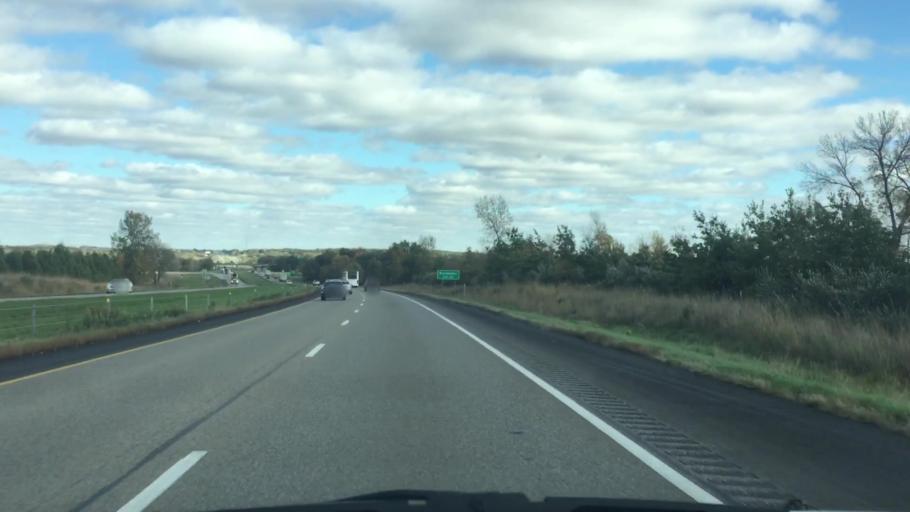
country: US
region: Iowa
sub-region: Muscatine County
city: West Liberty
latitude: 41.6465
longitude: -91.1646
